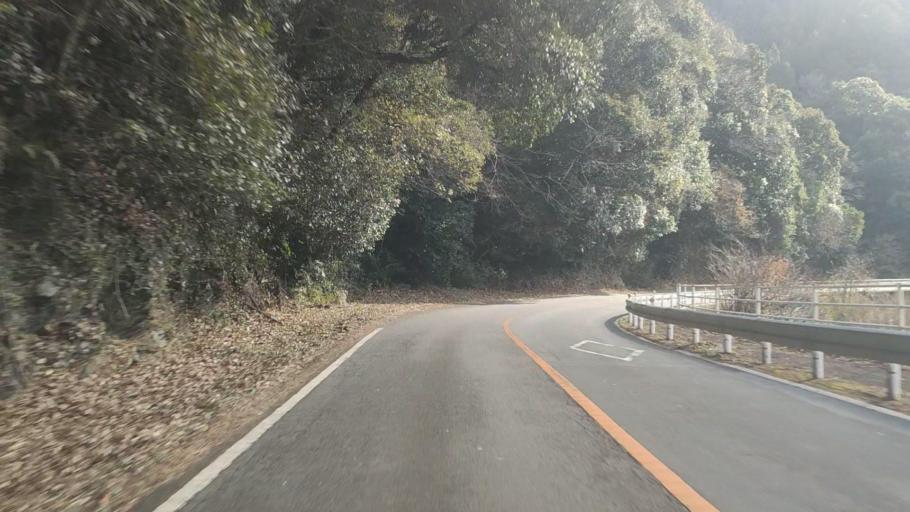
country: JP
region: Kumamoto
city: Hitoyoshi
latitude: 32.3019
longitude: 130.8454
